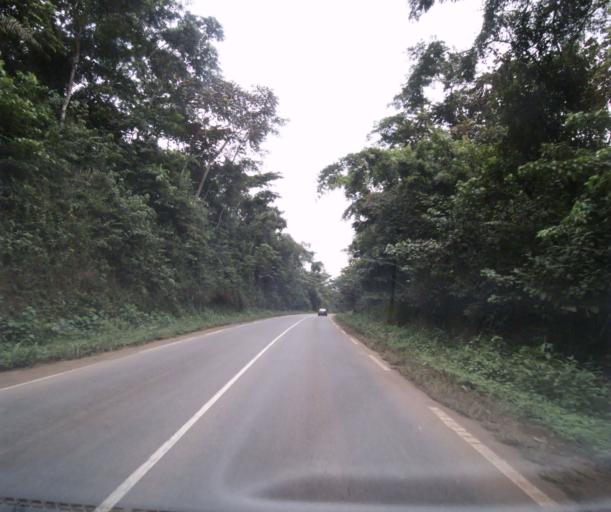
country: CM
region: Centre
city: Mbankomo
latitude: 3.7826
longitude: 11.2799
